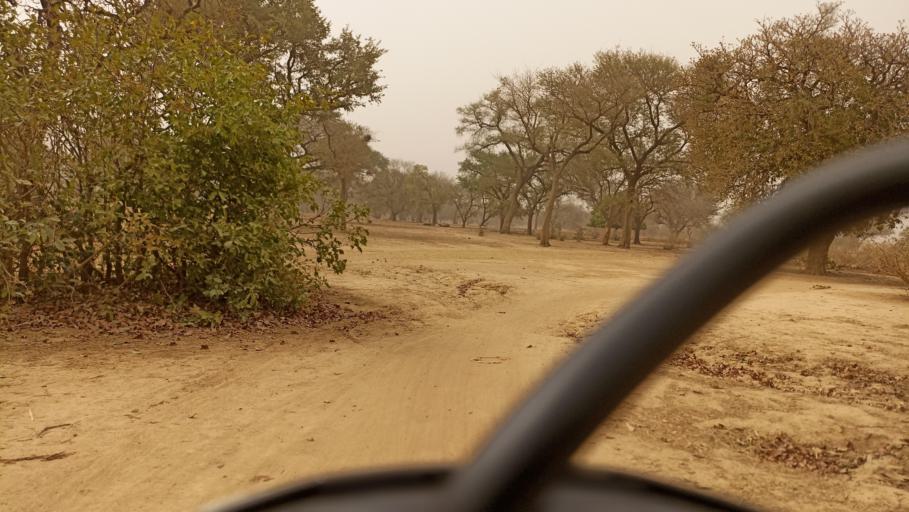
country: BF
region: Nord
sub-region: Province du Zondoma
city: Gourcy
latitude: 13.2750
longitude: -2.5366
